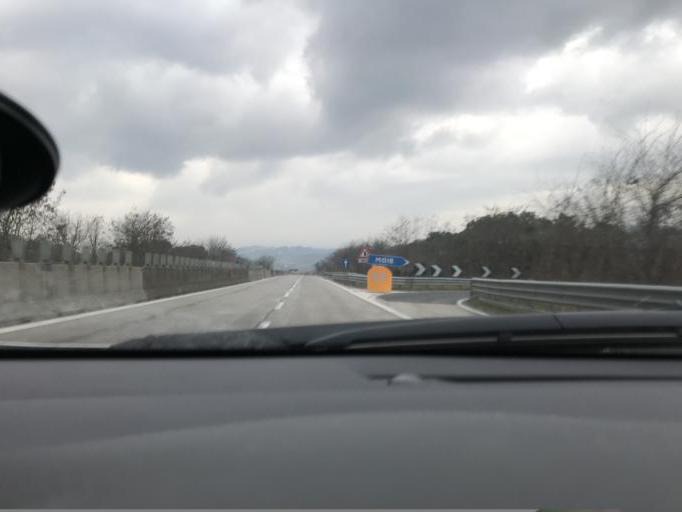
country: IT
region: The Marches
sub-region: Provincia di Ancona
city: Moie
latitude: 43.4949
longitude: 13.1284
